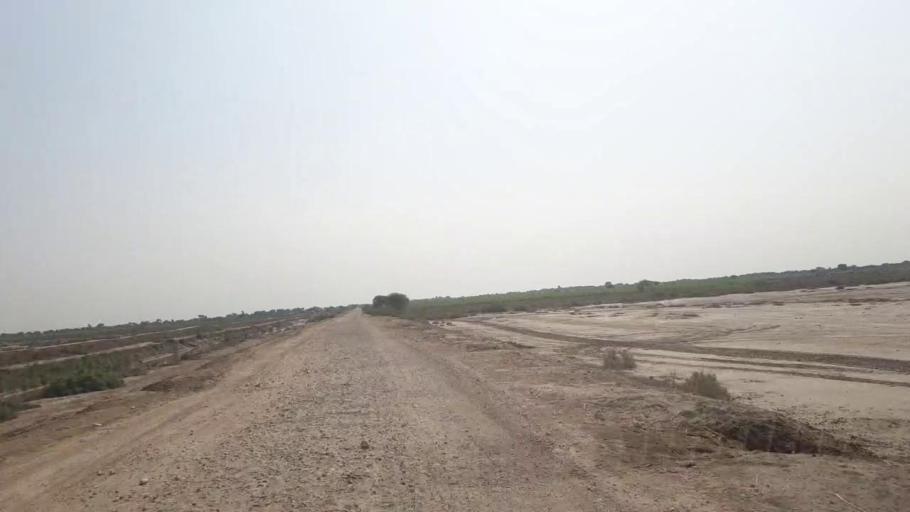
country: PK
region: Sindh
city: Kadhan
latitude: 24.4730
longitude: 68.9033
